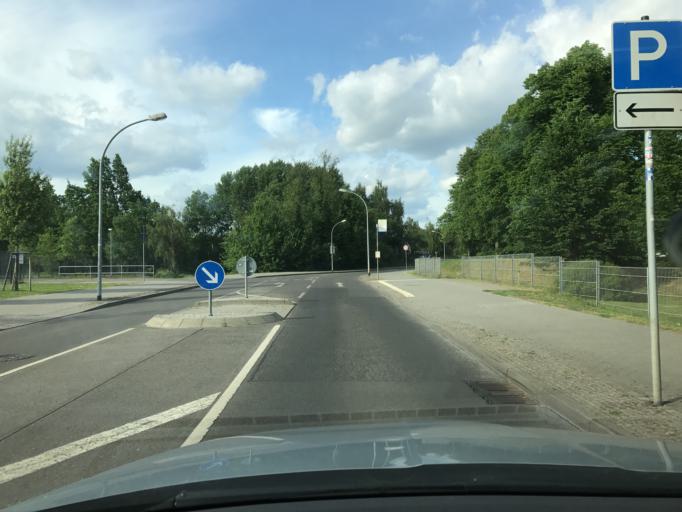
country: DE
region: Brandenburg
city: Falkensee
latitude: 52.5639
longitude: 13.0788
